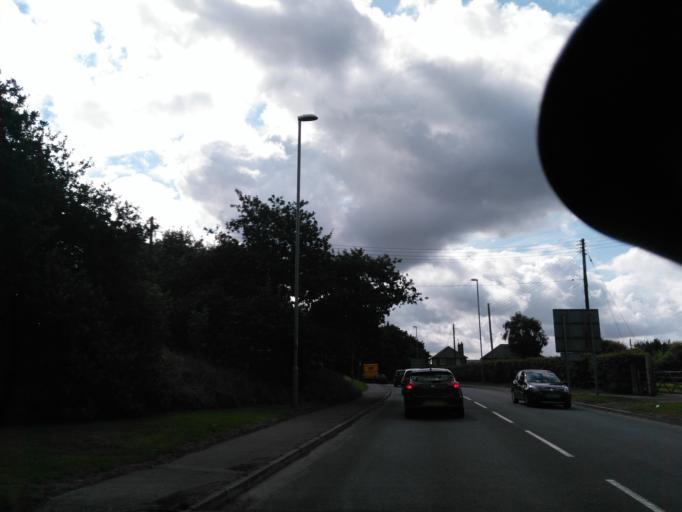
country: GB
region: England
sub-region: Dorset
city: Shaftesbury
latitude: 51.0096
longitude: -2.1928
